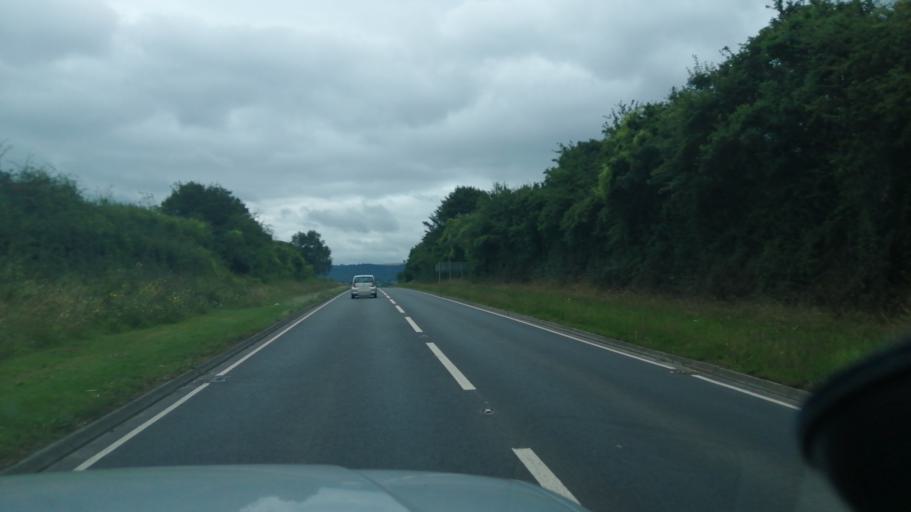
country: GB
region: England
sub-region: Herefordshire
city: Thruxton
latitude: 51.9954
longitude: -2.7913
